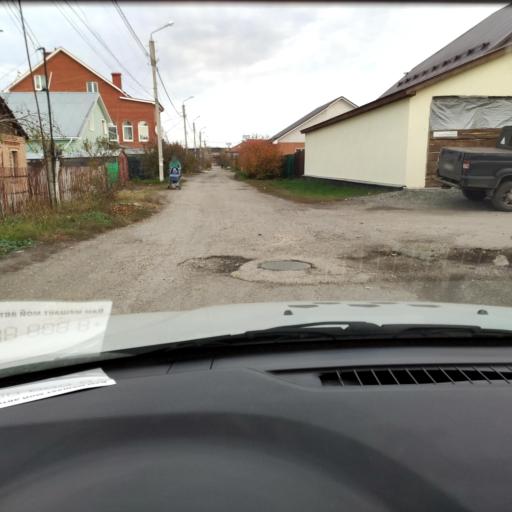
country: RU
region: Samara
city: Tol'yatti
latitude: 53.5104
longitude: 49.3980
